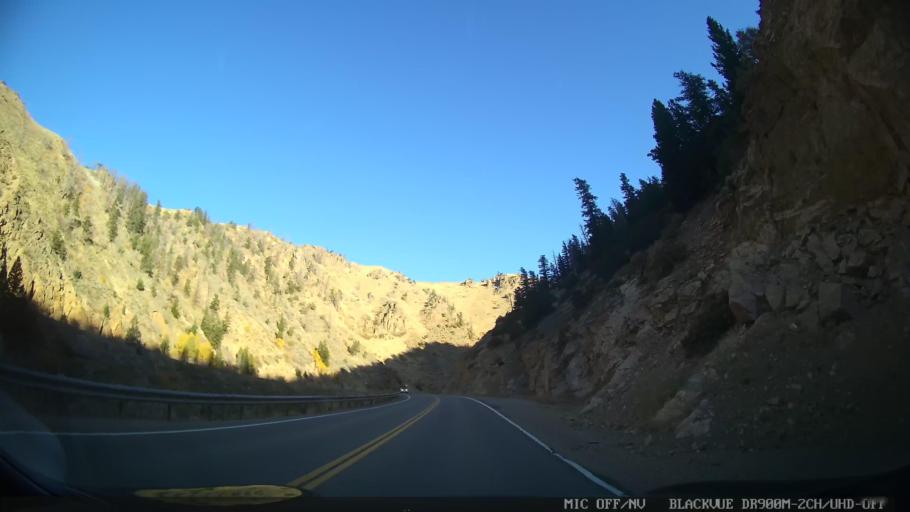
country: US
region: Colorado
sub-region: Grand County
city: Hot Sulphur Springs
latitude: 40.0561
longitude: -106.1339
